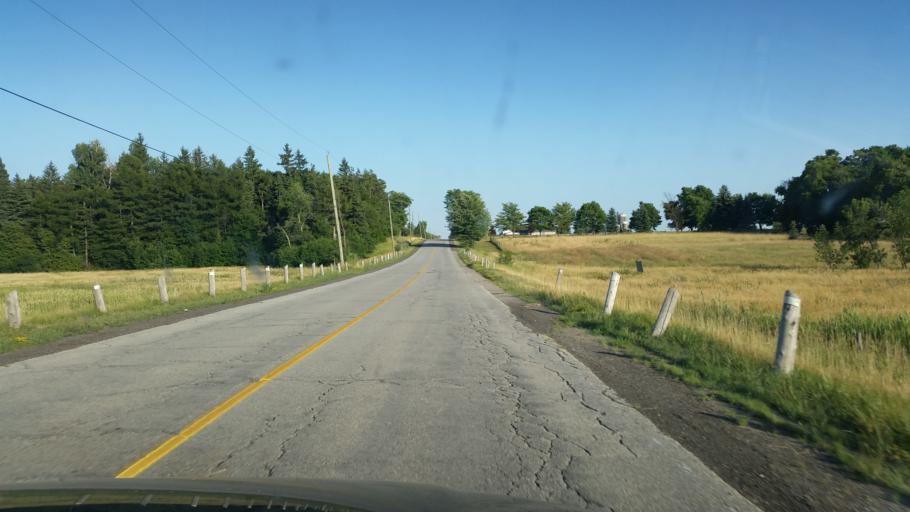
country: CA
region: Ontario
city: Brampton
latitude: 43.7681
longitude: -79.8241
